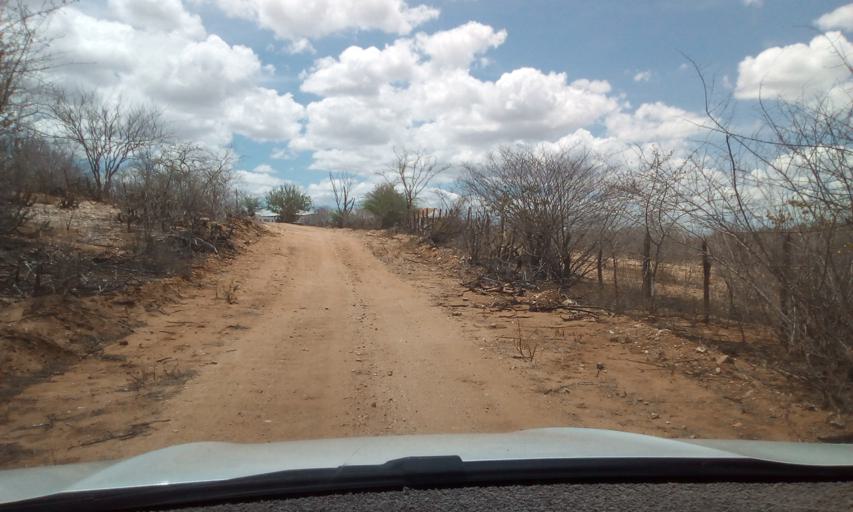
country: BR
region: Paraiba
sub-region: Picui
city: Picui
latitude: -6.5247
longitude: -36.3255
